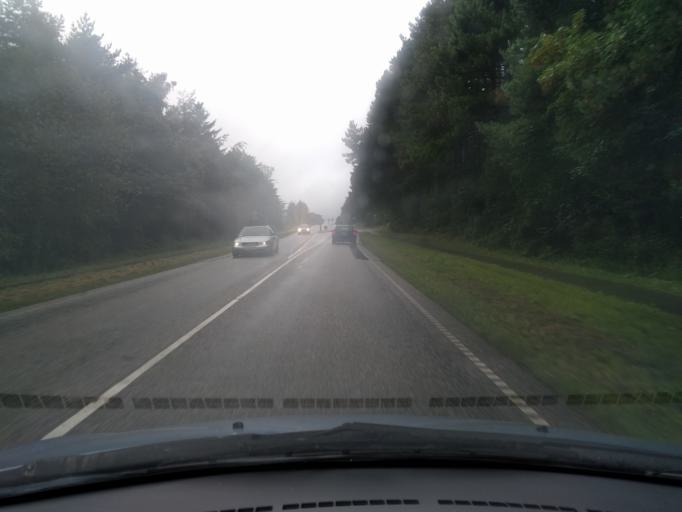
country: DK
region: Zealand
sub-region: Naestved Kommune
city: Naestved
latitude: 55.1744
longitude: 11.8009
